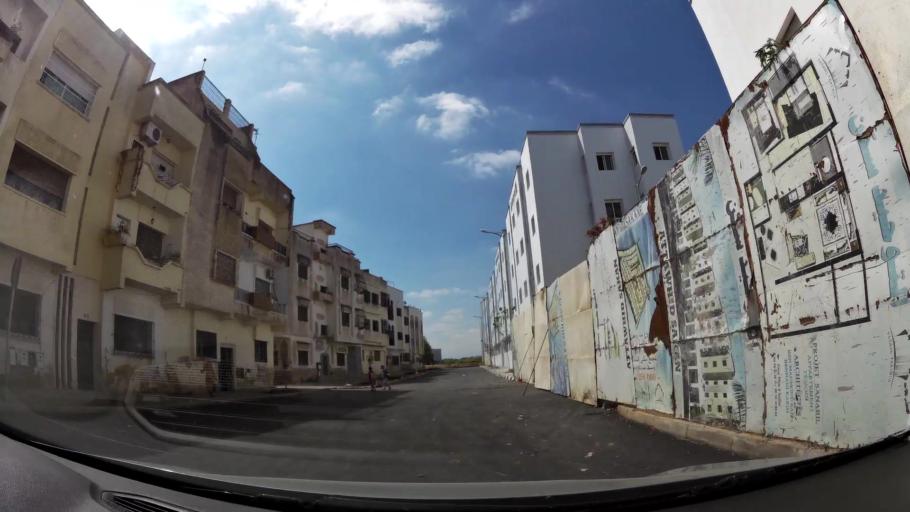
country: MA
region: Fes-Boulemane
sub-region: Fes
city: Fes
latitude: 34.0394
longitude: -5.0322
